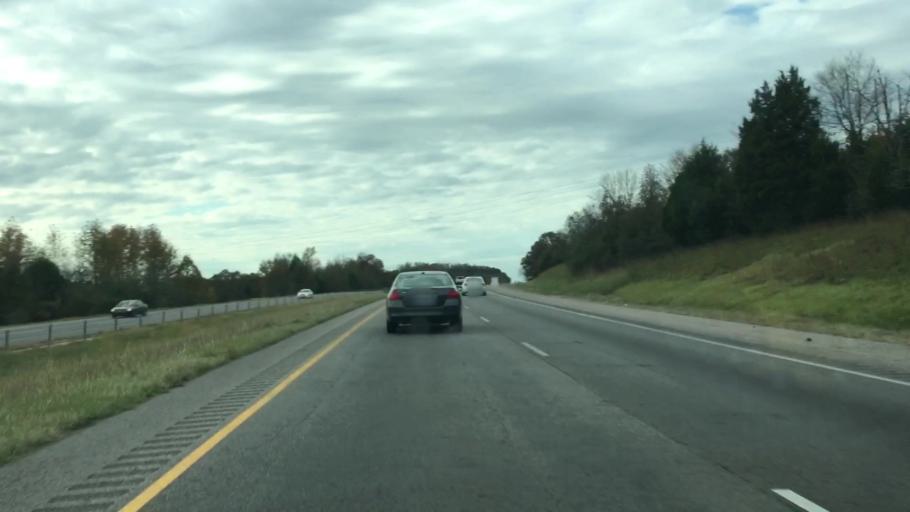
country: US
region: Arkansas
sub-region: Conway County
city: Morrilton
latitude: 35.1639
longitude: -92.6790
